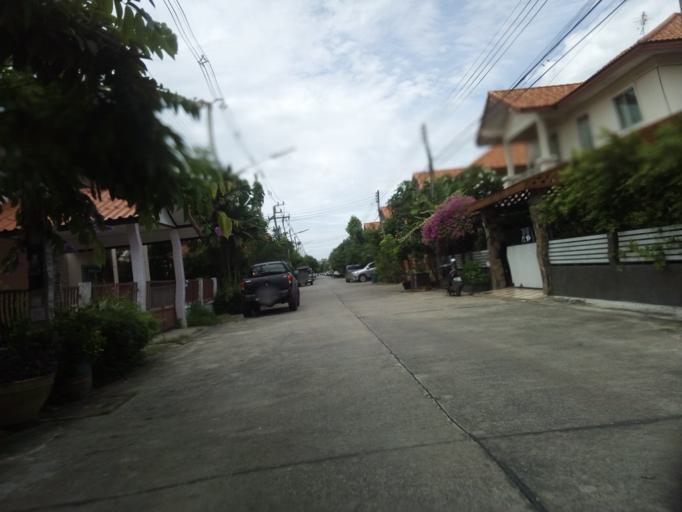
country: TH
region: Pathum Thani
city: Ban Rangsit
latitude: 14.0513
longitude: 100.8349
